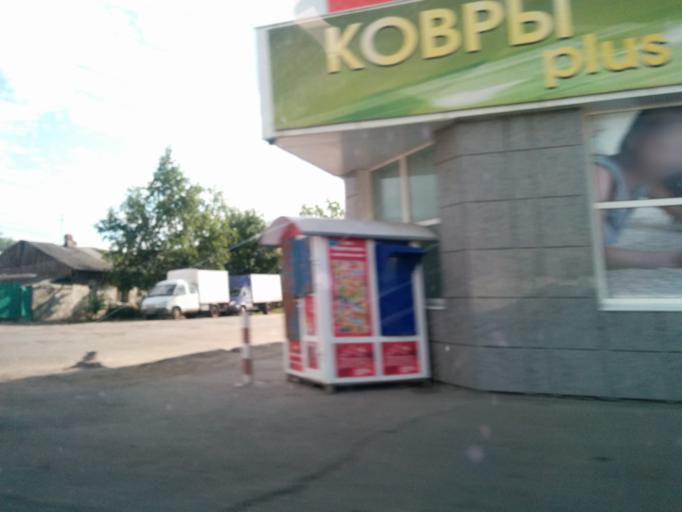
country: RU
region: Tambov
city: Tambov
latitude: 52.7228
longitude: 41.4370
